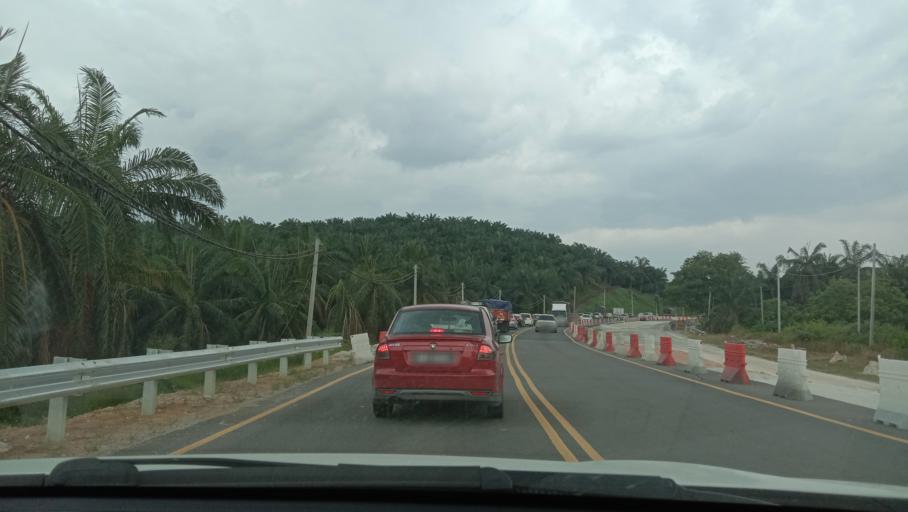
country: MY
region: Selangor
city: Batu Arang
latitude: 3.2625
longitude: 101.4612
